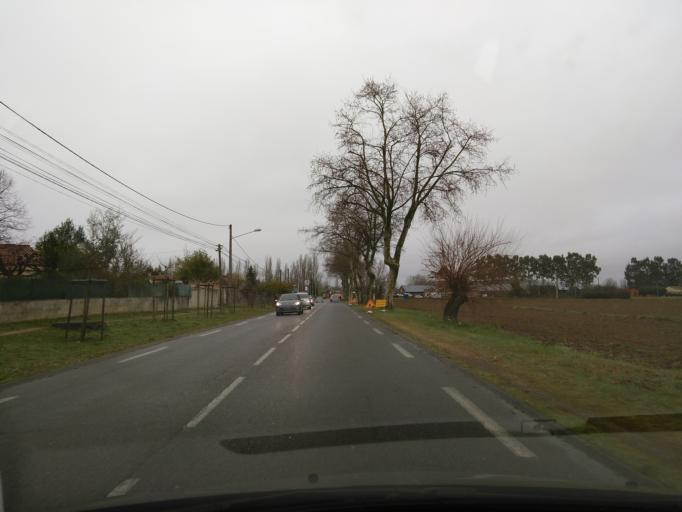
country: FR
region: Midi-Pyrenees
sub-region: Departement de la Haute-Garonne
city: Rieux-Volvestre
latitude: 43.2628
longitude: 1.1939
